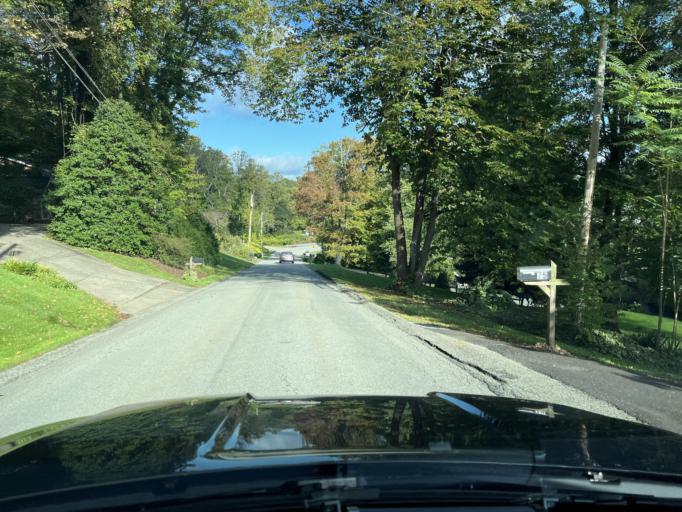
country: US
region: Pennsylvania
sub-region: Fayette County
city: South Uniontown
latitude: 39.8911
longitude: -79.7569
